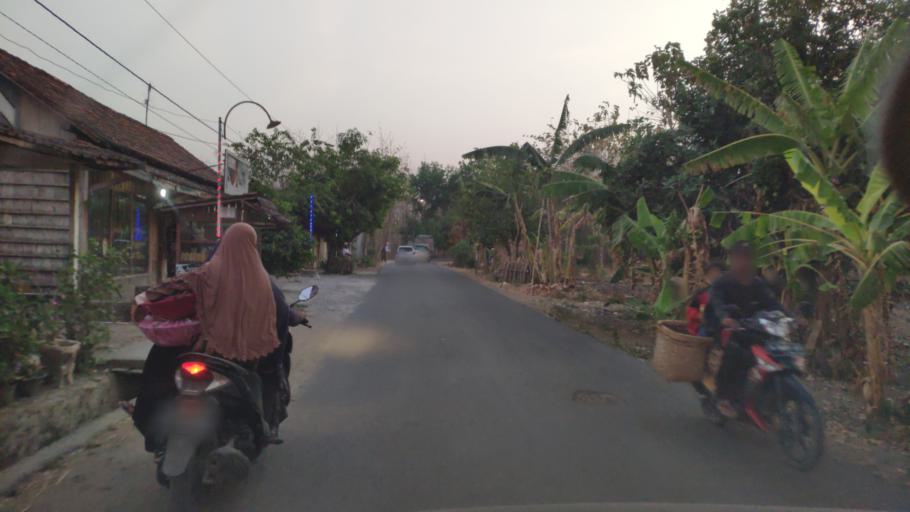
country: ID
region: Central Java
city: Ngliron
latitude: -7.1390
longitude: 111.4225
